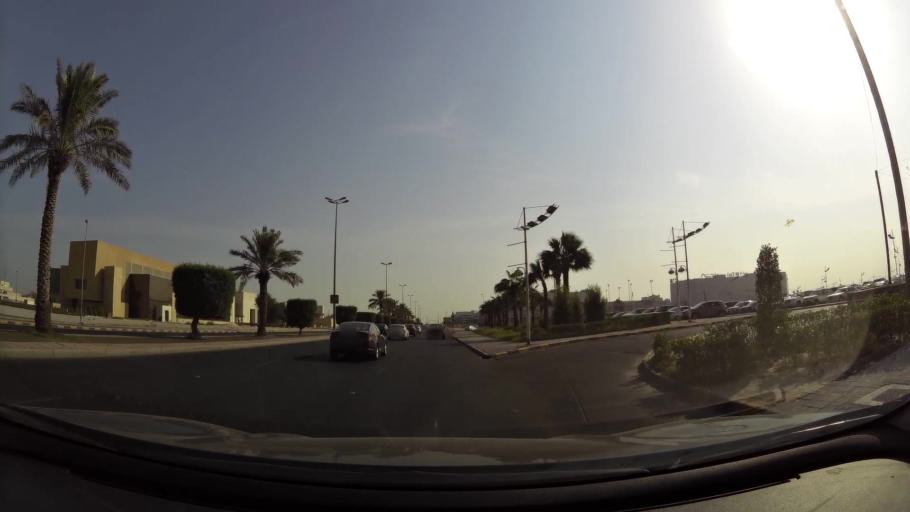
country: KW
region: Mubarak al Kabir
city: Mubarak al Kabir
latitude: 29.1732
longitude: 48.0998
